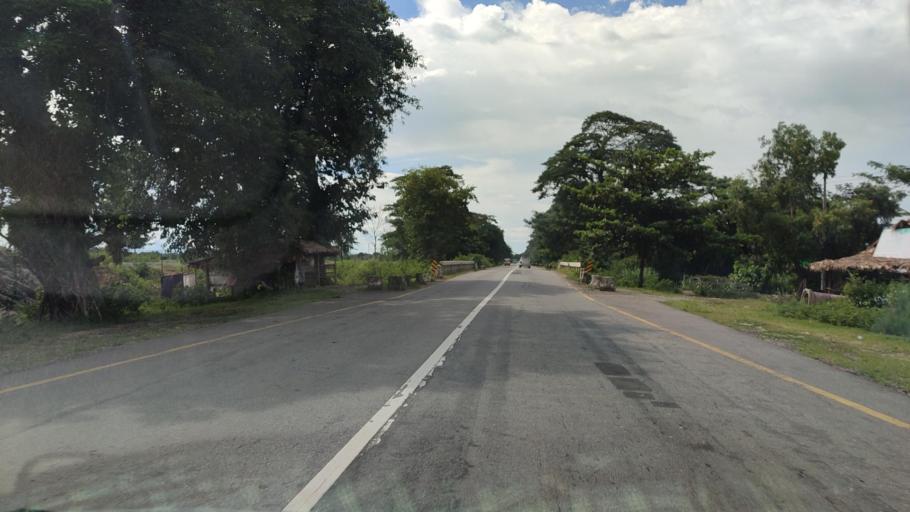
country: MM
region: Bago
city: Nyaunglebin
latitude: 18.1723
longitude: 96.6006
